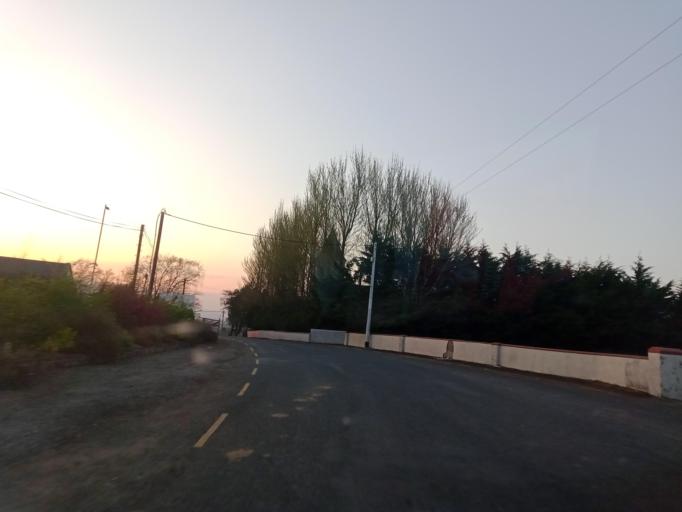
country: IE
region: Leinster
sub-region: Laois
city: Abbeyleix
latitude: 52.9643
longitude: -7.3680
